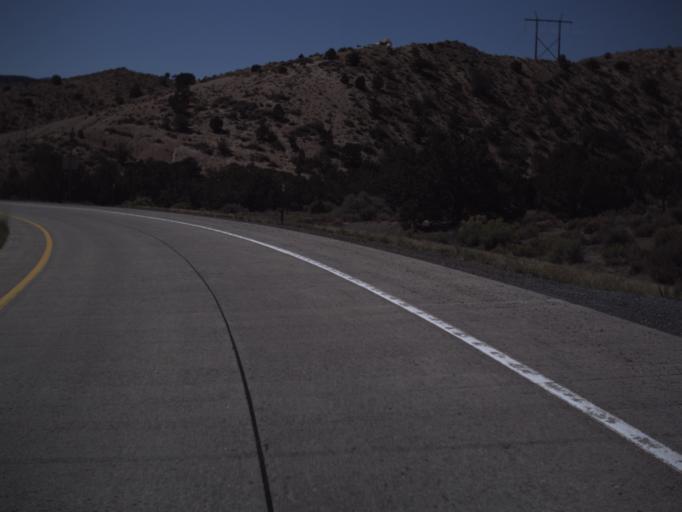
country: US
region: Utah
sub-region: Sevier County
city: Monroe
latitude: 38.6031
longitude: -112.2535
